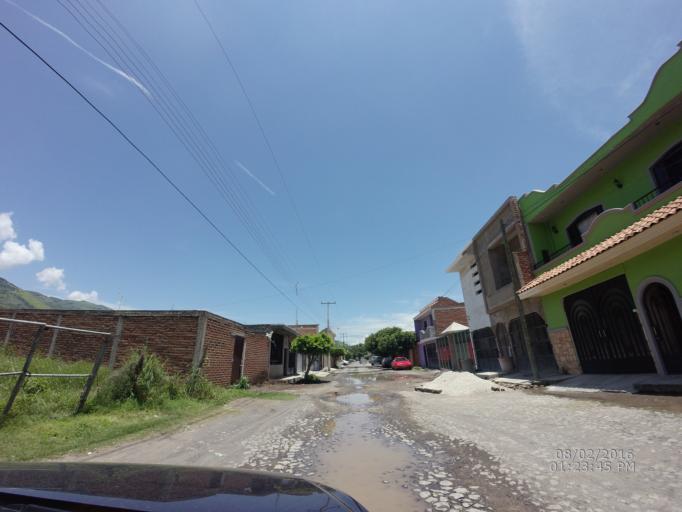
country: MX
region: Nayarit
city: Ixtlan del Rio
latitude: 21.0391
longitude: -104.3783
